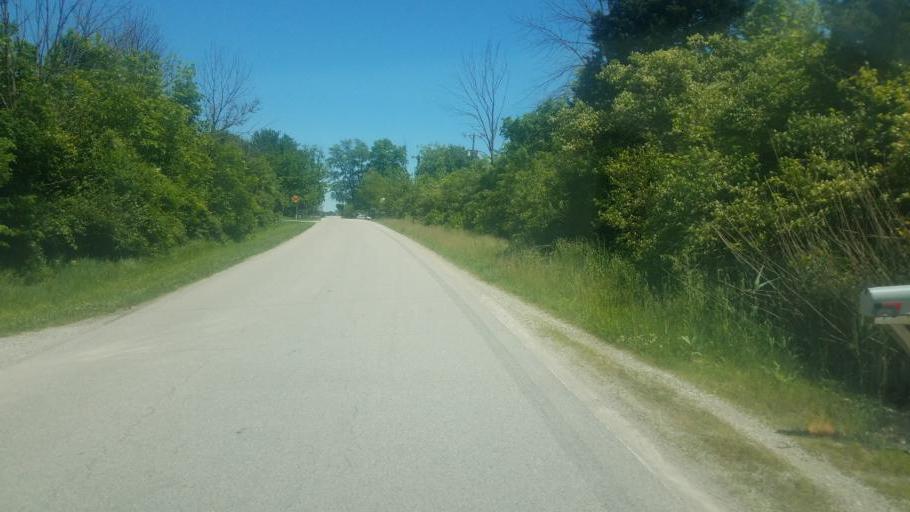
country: US
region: Ohio
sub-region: Shelby County
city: Sidney
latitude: 40.2162
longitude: -84.2005
